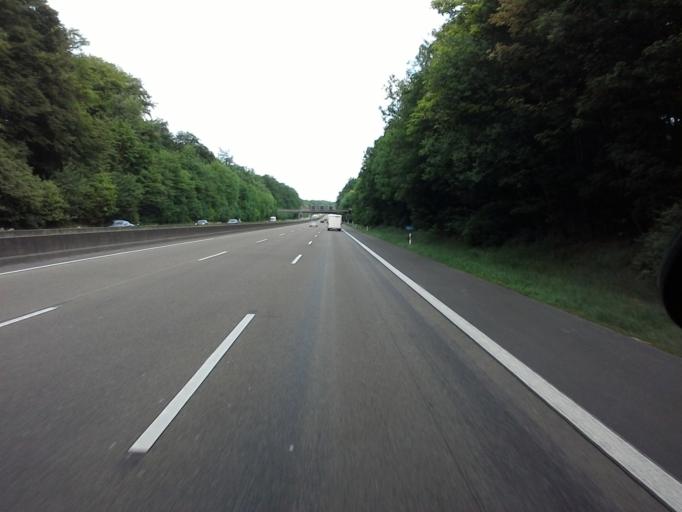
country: DE
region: Hesse
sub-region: Regierungsbezirk Darmstadt
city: Seligenstadt
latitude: 50.0151
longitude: 8.9644
